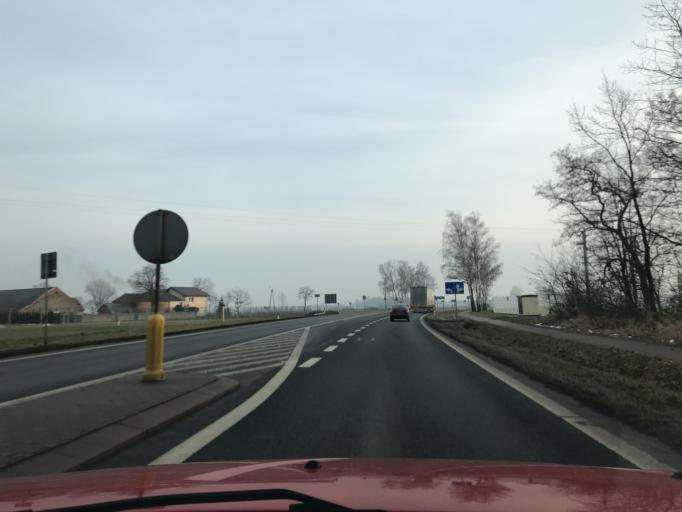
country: PL
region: Greater Poland Voivodeship
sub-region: Powiat pleszewski
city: Goluchow
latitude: 51.8218
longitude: 17.9733
